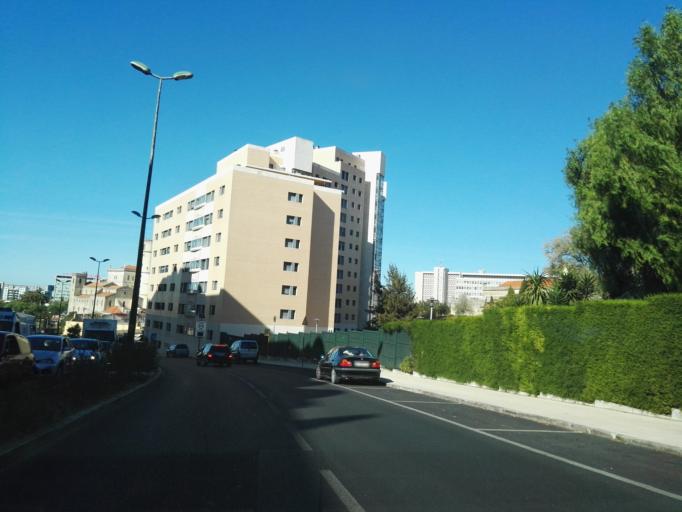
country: PT
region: Lisbon
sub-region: Lisbon
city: Lisbon
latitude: 38.7298
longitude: -9.1615
